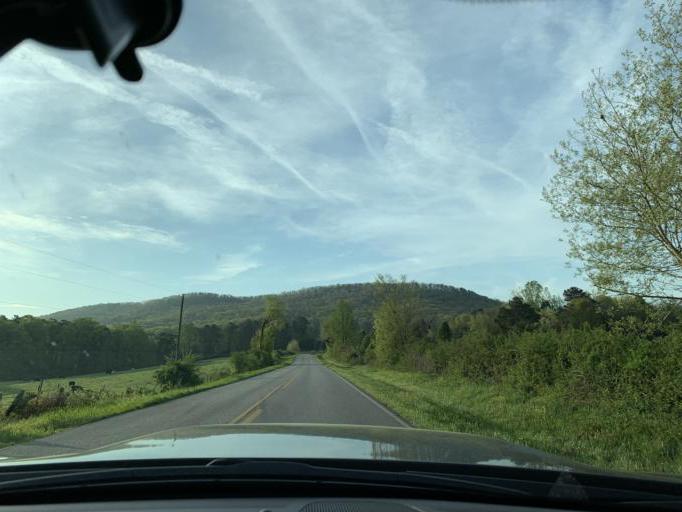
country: US
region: Georgia
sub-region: Forsyth County
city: Cumming
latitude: 34.2572
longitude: -84.1461
